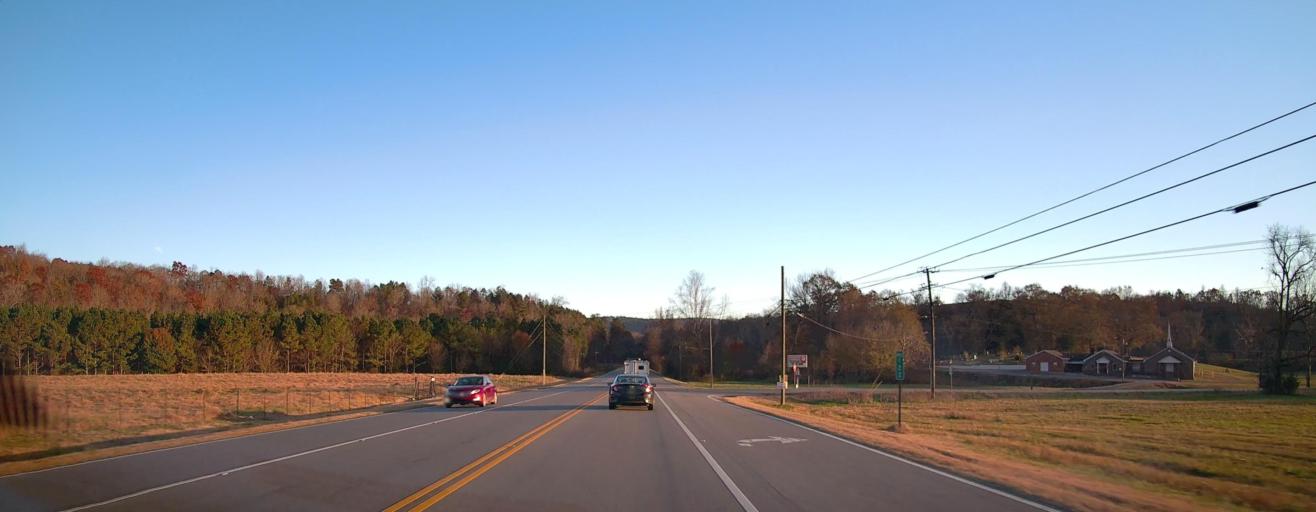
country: US
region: Alabama
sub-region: Etowah County
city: Attalla
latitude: 34.0478
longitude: -86.1582
